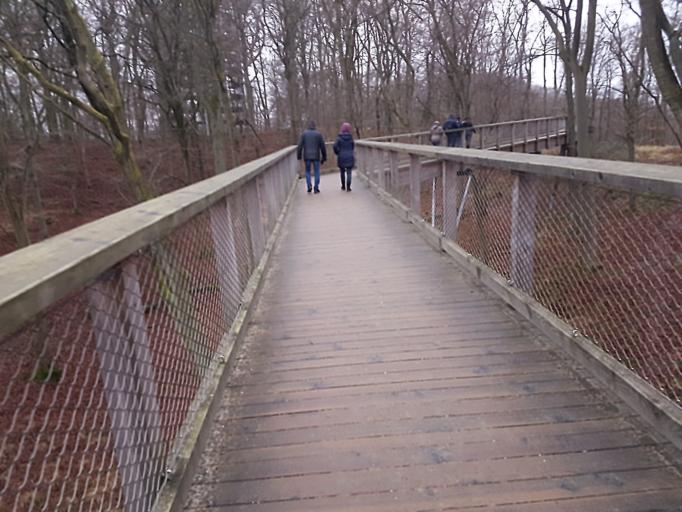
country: DE
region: Mecklenburg-Vorpommern
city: Ostseebad Binz
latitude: 54.4321
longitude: 13.5599
